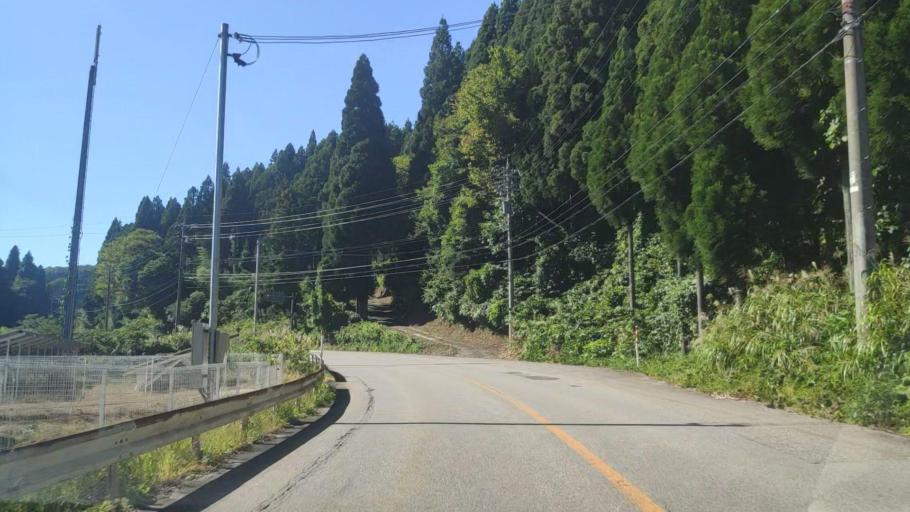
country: JP
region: Ishikawa
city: Nanao
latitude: 37.3217
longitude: 137.1838
